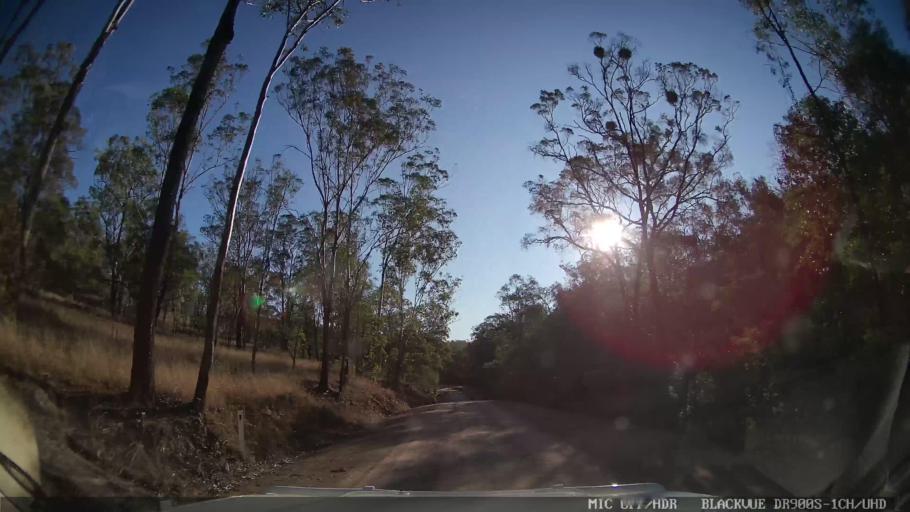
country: AU
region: Queensland
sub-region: Gladstone
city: Toolooa
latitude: -24.6953
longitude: 151.4074
